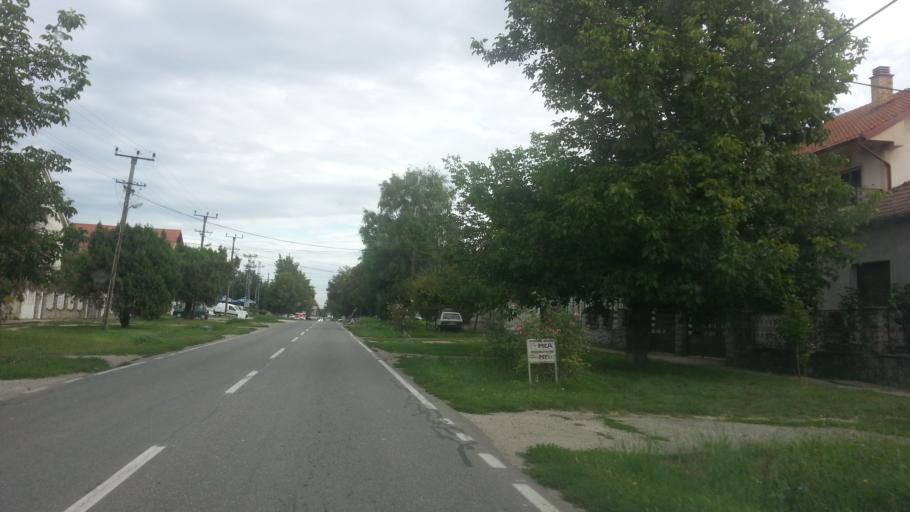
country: RS
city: Novi Banovci
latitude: 44.9613
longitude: 20.2812
